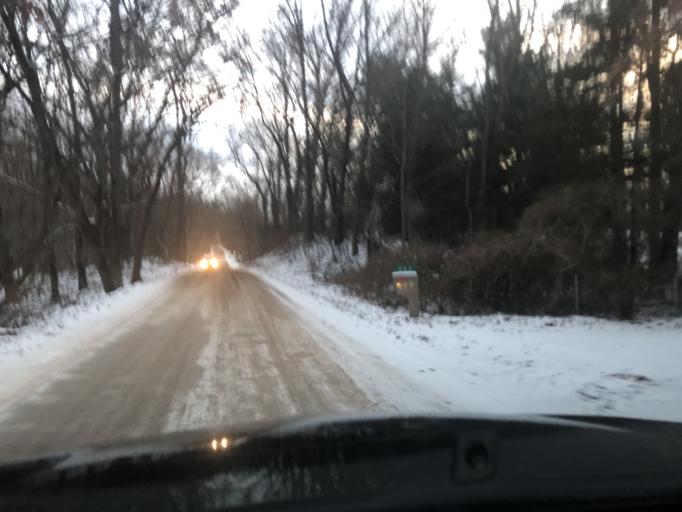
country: US
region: Michigan
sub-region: Oakland County
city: Milford
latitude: 42.5744
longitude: -83.6392
